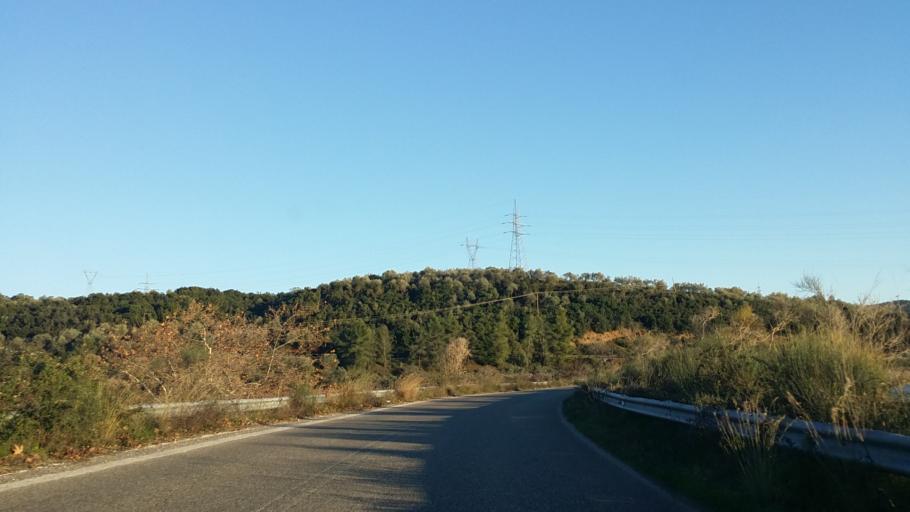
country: GR
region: West Greece
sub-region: Nomos Aitolias kai Akarnanias
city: Neapolis
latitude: 38.7132
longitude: 21.3406
